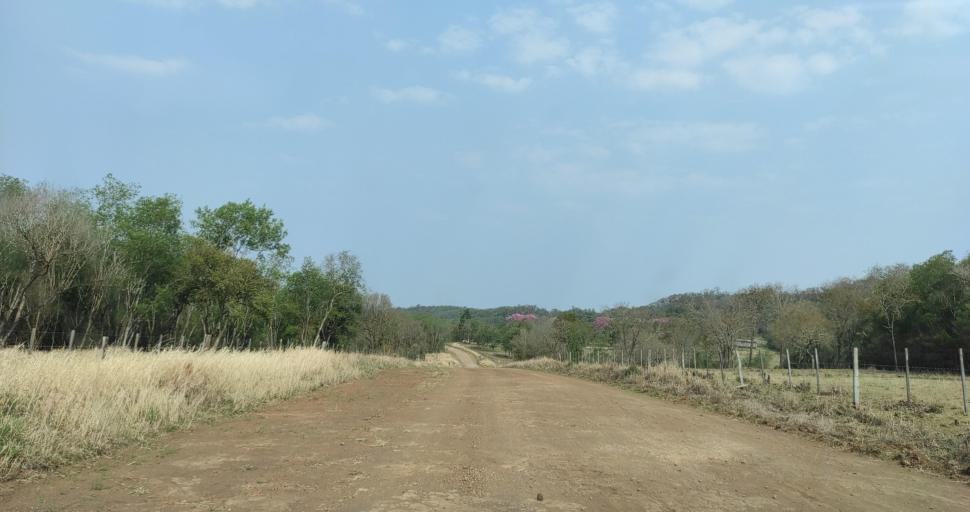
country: AR
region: Misiones
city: Cerro Azul
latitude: -27.6084
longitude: -55.5695
